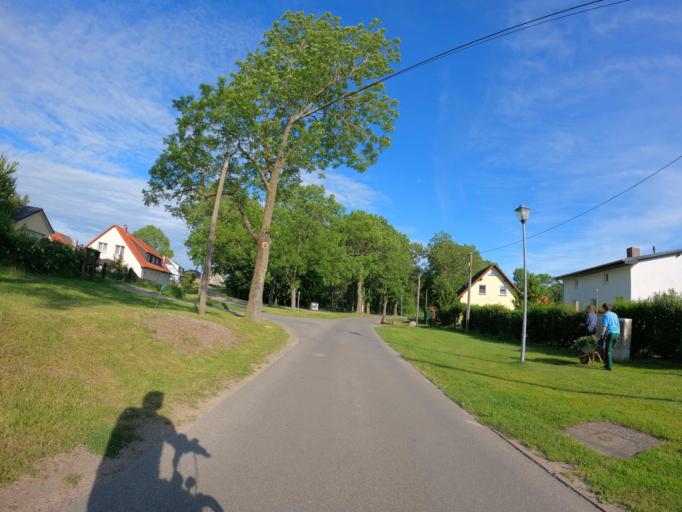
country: DE
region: Mecklenburg-Vorpommern
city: Preetz
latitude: 54.3303
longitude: 12.9733
